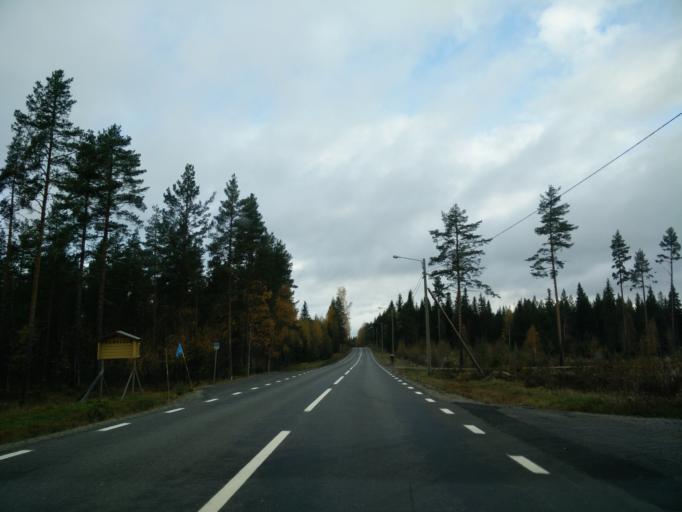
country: SE
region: Jaemtland
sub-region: Braecke Kommun
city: Braecke
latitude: 62.3955
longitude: 15.2209
